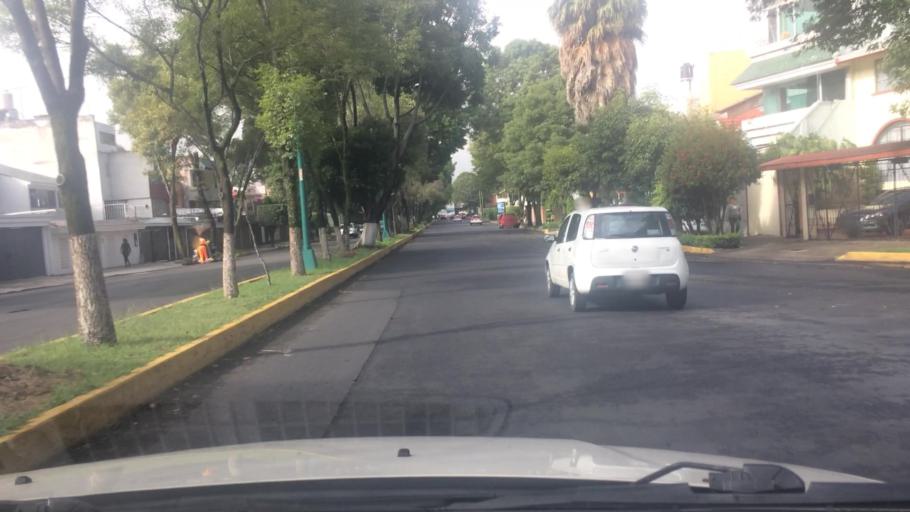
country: MX
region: Mexico City
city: Coyoacan
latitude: 19.3416
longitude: -99.1268
